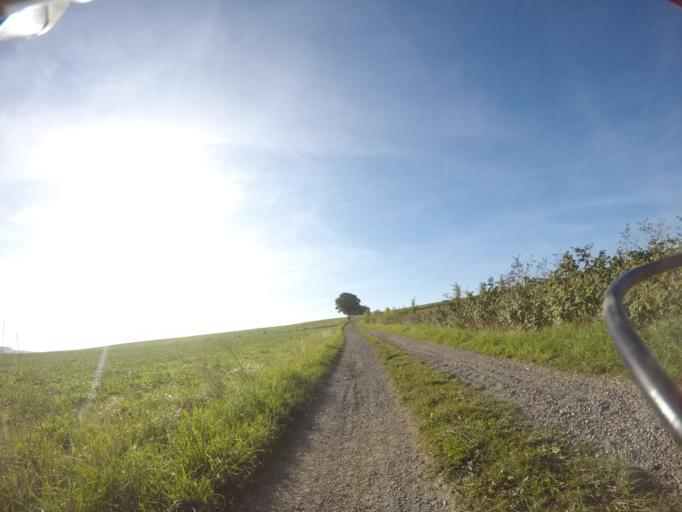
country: BE
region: Wallonia
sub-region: Province du Luxembourg
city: Fauvillers
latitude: 49.9142
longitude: 5.6593
